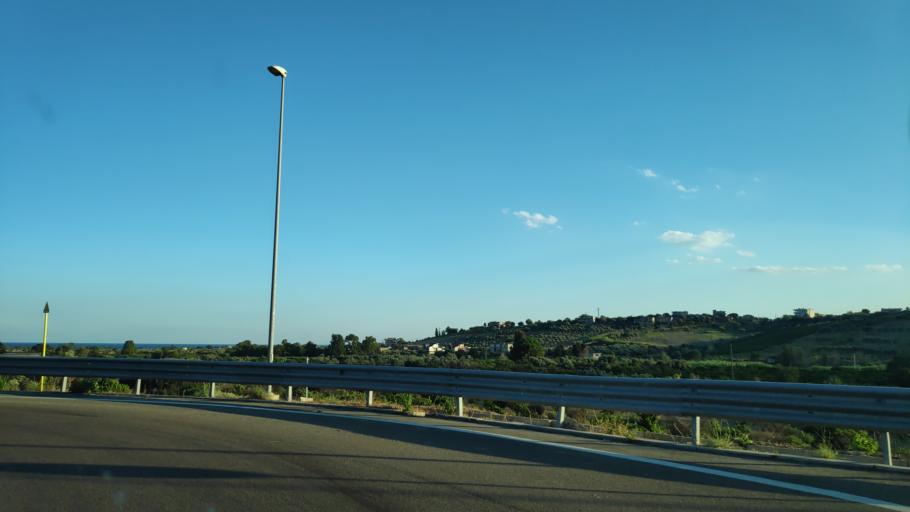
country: IT
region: Calabria
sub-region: Provincia di Reggio Calabria
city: Locri
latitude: 38.2366
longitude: 16.2380
